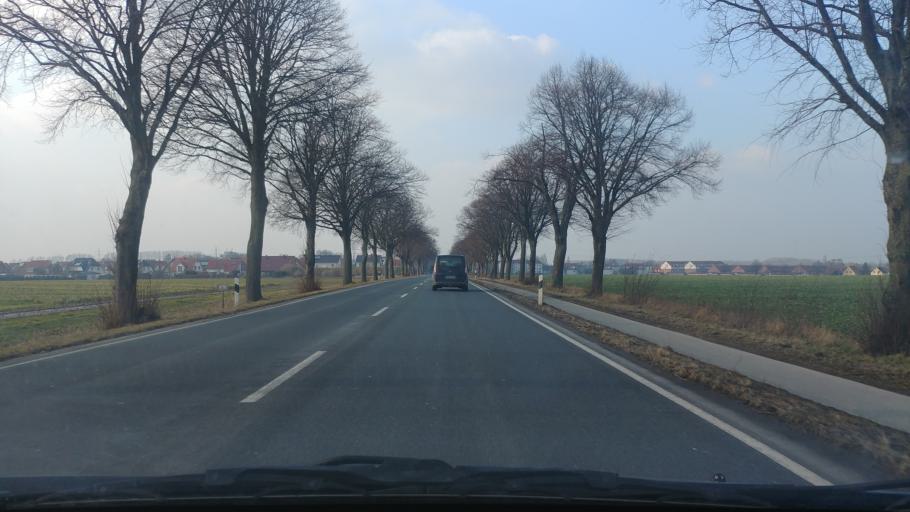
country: DE
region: Lower Saxony
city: Pattensen
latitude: 52.2913
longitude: 9.7504
